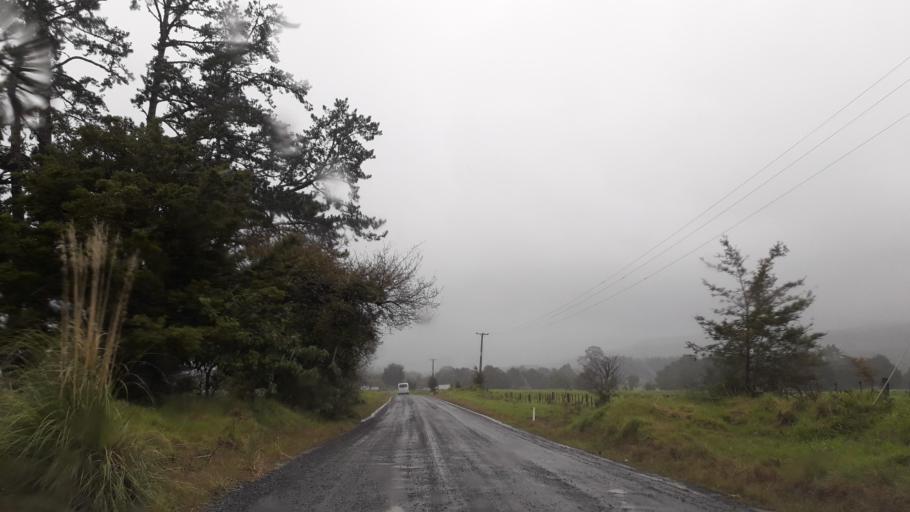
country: NZ
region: Northland
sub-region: Far North District
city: Waimate North
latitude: -35.4993
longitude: 173.6989
